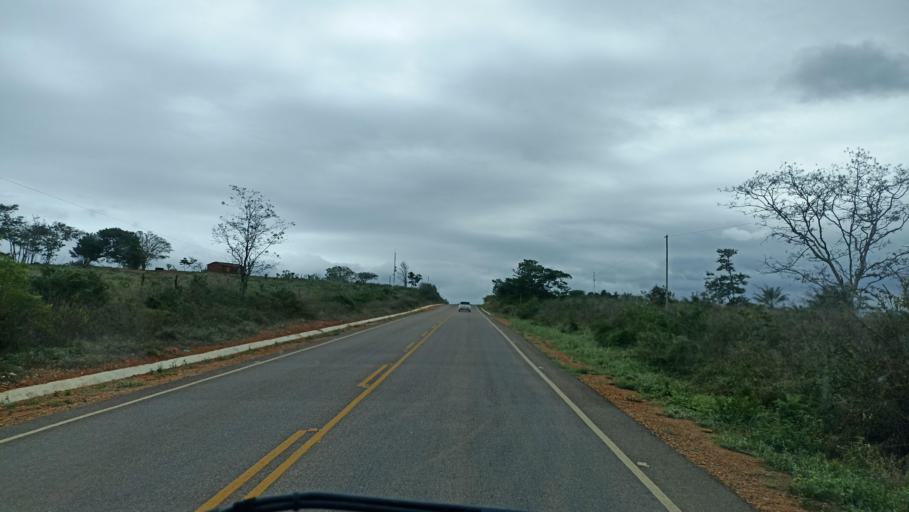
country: BR
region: Bahia
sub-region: Andarai
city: Vera Cruz
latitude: -12.9931
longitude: -40.9995
